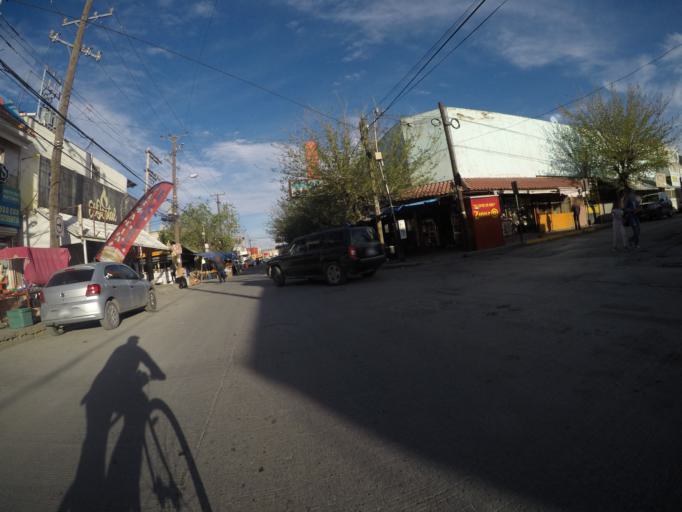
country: MX
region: Chihuahua
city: Ciudad Juarez
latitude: 31.7367
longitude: -106.4872
